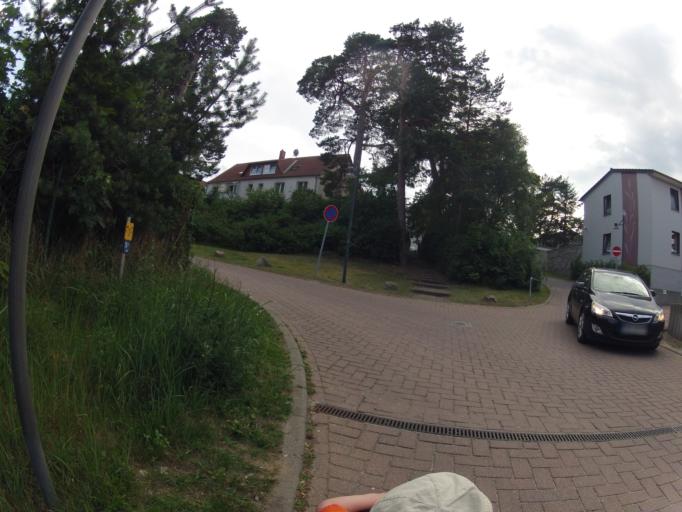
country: DE
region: Mecklenburg-Vorpommern
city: Seebad Heringsdorf
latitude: 53.9370
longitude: 14.1964
